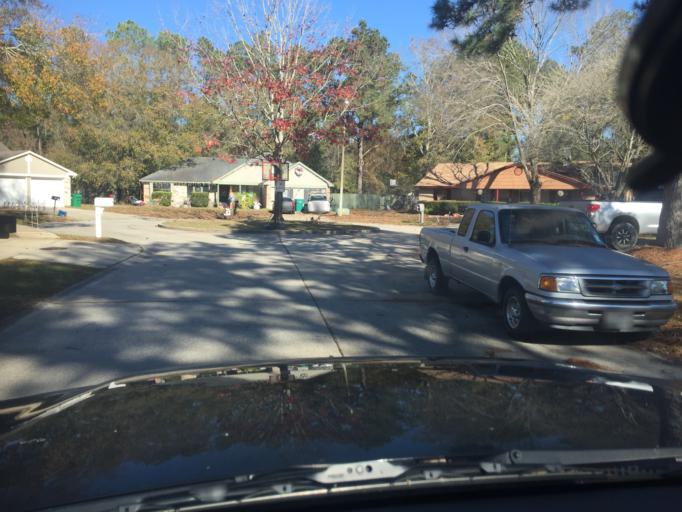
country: US
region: Louisiana
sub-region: Saint Tammany Parish
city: Slidell
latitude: 30.3022
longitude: -89.7327
